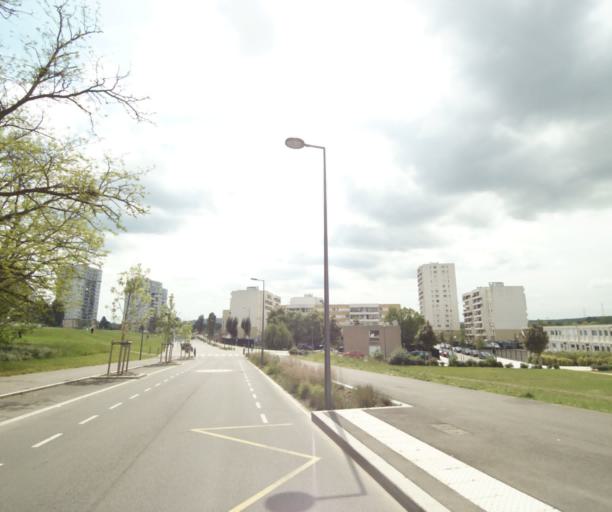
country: FR
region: Ile-de-France
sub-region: Departement des Yvelines
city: Les Mureaux
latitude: 48.9789
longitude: 1.9182
